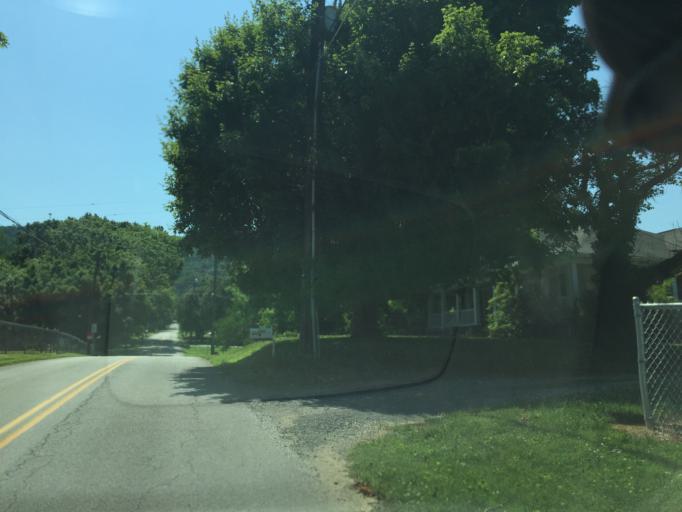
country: US
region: Tennessee
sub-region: Hamilton County
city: Collegedale
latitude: 35.0743
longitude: -85.0600
